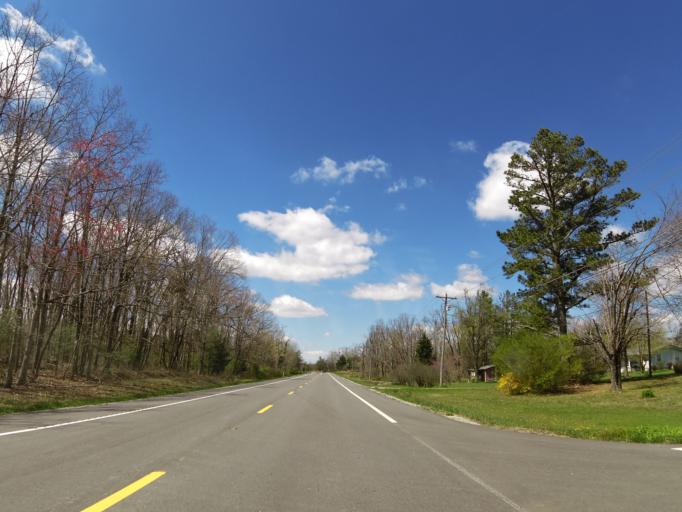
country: US
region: Tennessee
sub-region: Putnam County
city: Monterey
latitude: 35.9656
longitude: -85.2499
